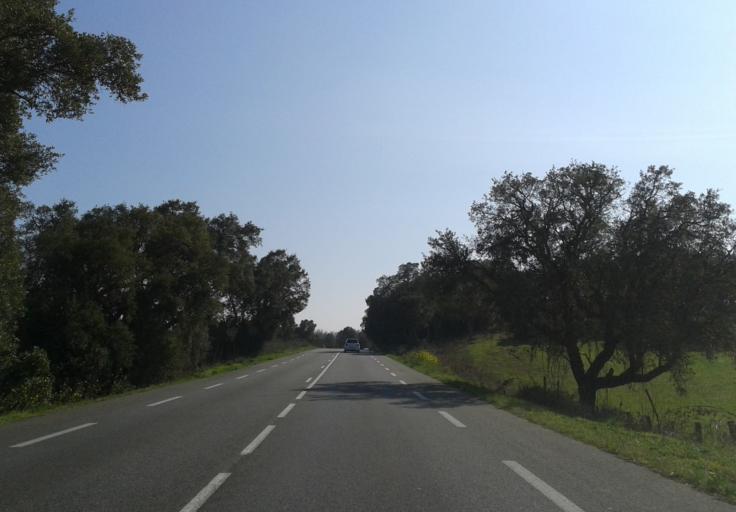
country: FR
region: Corsica
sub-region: Departement de la Haute-Corse
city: Linguizzetta
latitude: 42.2379
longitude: 9.5456
